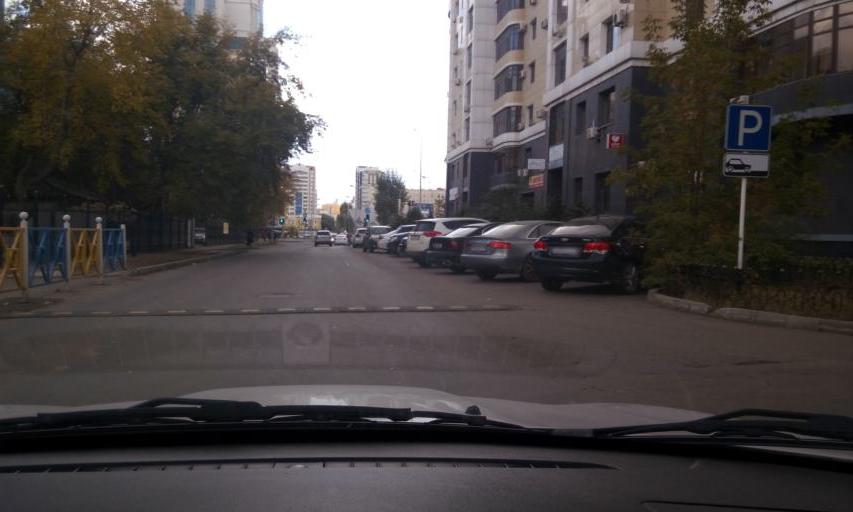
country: KZ
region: Astana Qalasy
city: Astana
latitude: 51.1672
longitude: 71.4312
